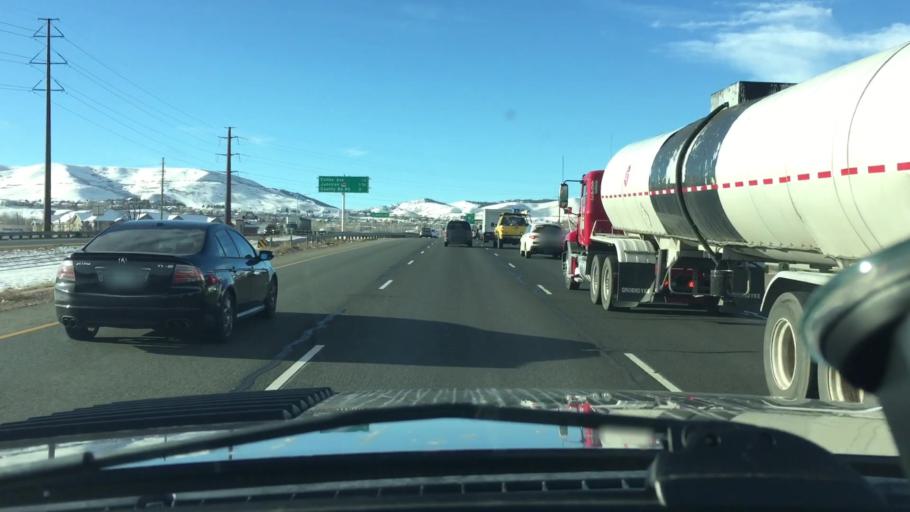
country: US
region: Colorado
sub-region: Jefferson County
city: West Pleasant View
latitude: 39.7363
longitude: -105.1667
